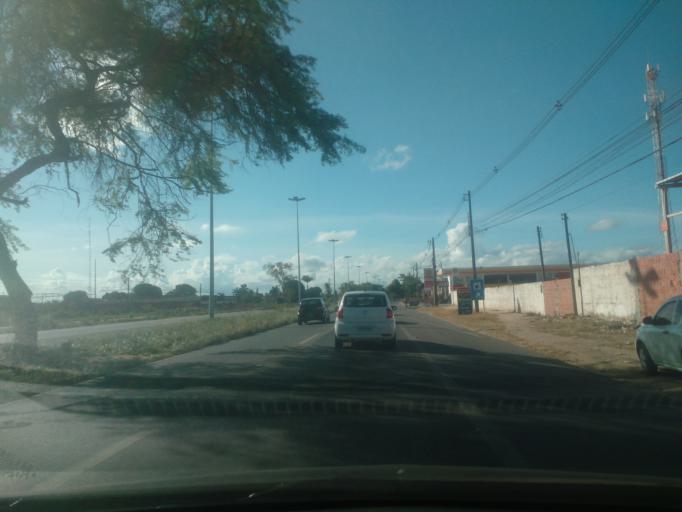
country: BR
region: Alagoas
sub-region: Satuba
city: Satuba
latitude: -9.5298
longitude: -35.7973
